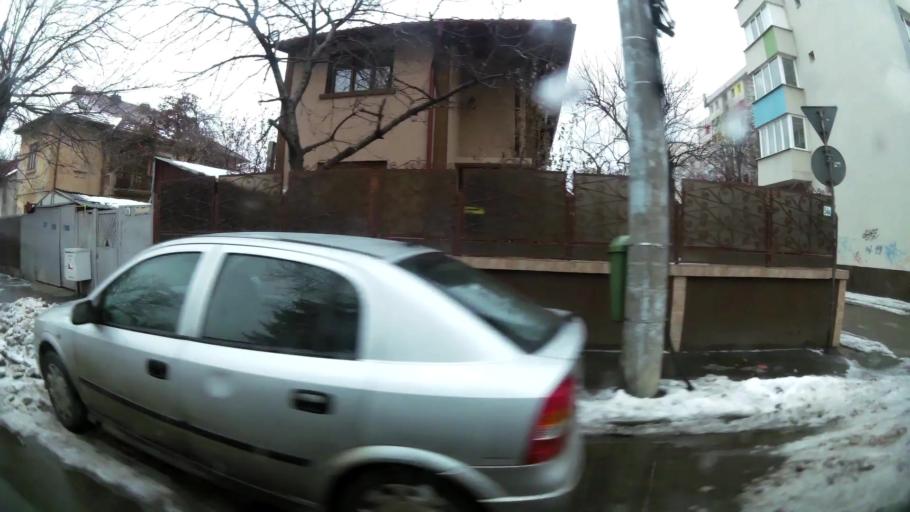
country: RO
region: Ilfov
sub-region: Comuna Chiajna
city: Rosu
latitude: 44.4744
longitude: 26.0485
